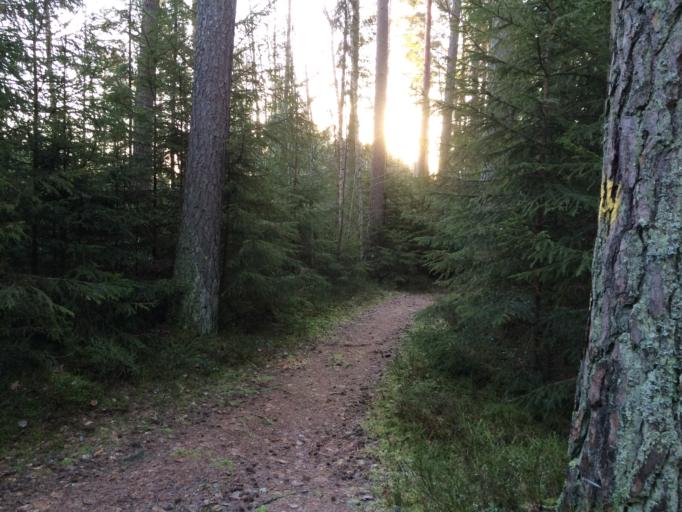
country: SE
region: Vaestmanland
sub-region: Hallstahammars Kommun
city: Hallstahammar
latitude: 59.6217
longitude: 16.1983
